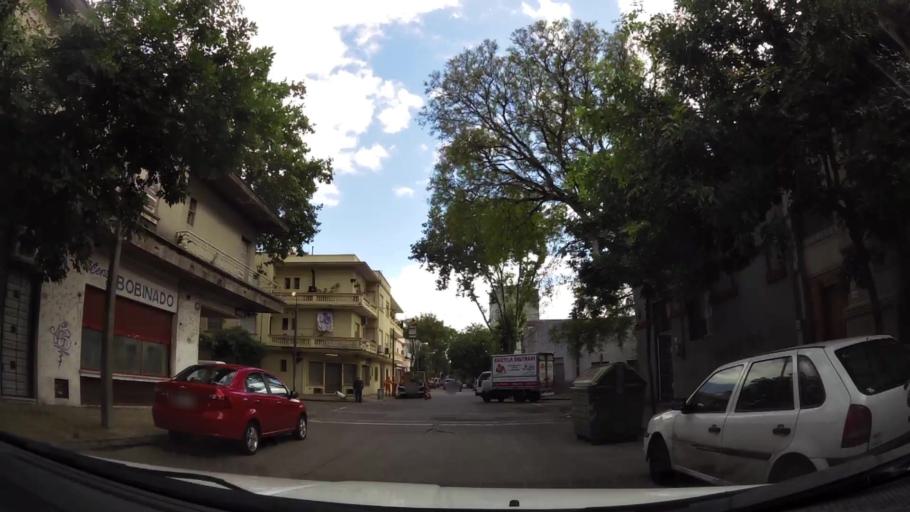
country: UY
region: Montevideo
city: Montevideo
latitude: -34.8847
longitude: -56.1829
